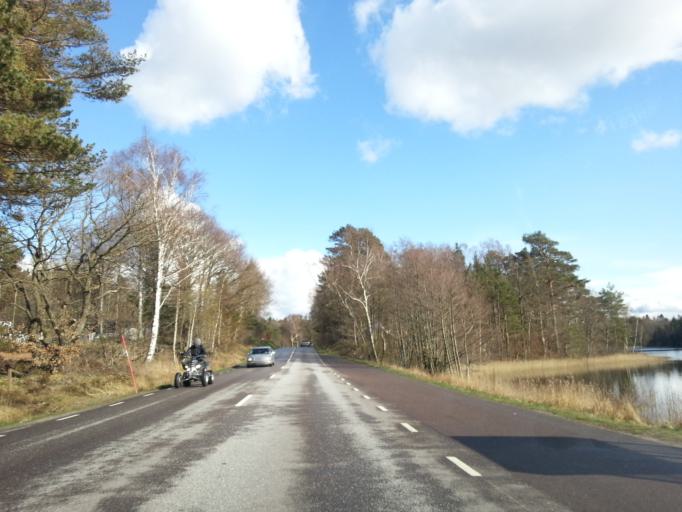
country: SE
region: Vaestra Goetaland
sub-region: Kungalvs Kommun
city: Kode
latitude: 57.9320
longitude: 11.8902
